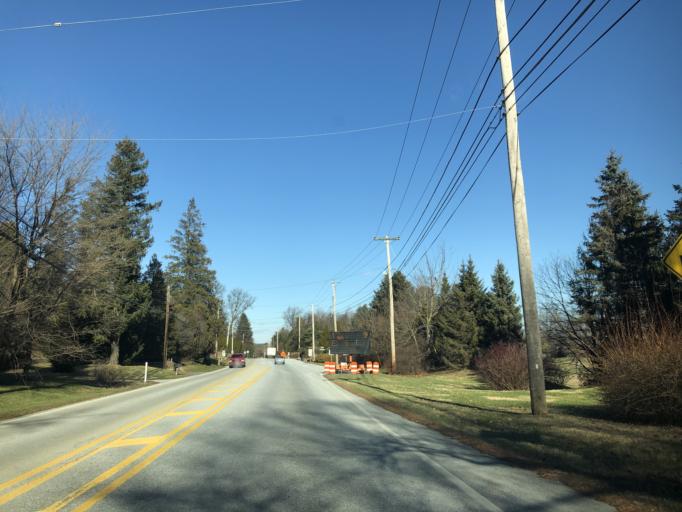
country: US
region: Pennsylvania
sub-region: Chester County
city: Kennett Square
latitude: 39.8673
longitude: -75.7170
